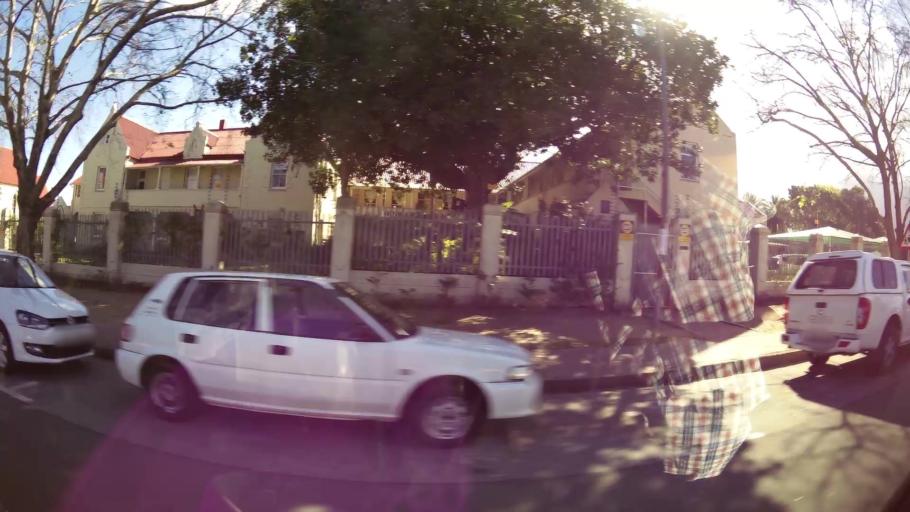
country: ZA
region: Western Cape
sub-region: Eden District Municipality
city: George
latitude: -33.9595
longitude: 22.4604
